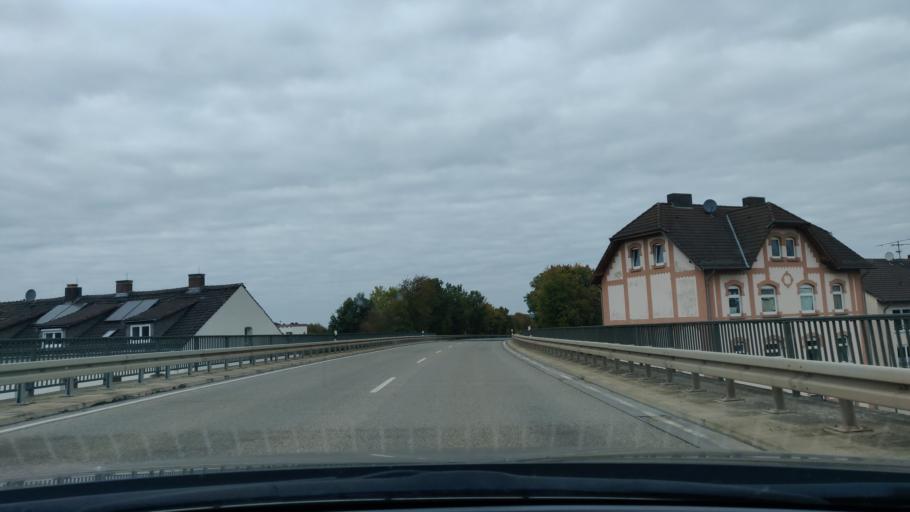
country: DE
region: Hesse
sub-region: Regierungsbezirk Kassel
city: Wabern
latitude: 51.1025
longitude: 9.3569
